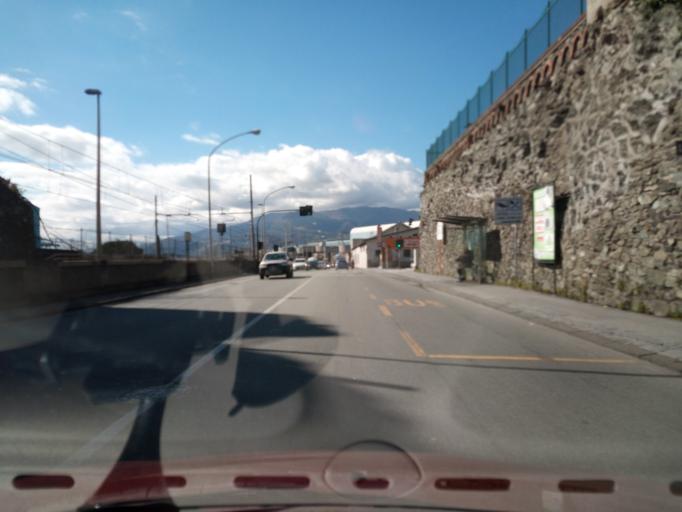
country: IT
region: Liguria
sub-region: Provincia di Genova
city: Mele
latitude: 44.4248
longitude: 8.7998
